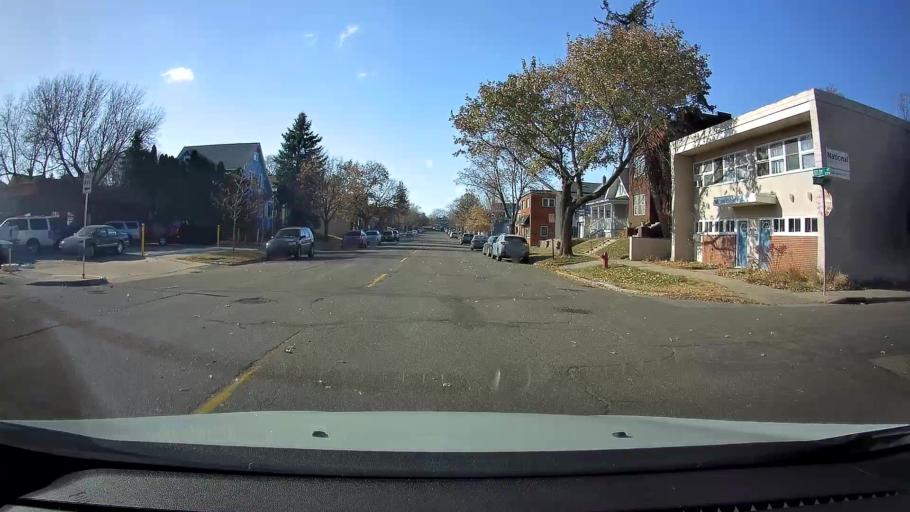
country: US
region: Minnesota
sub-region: Ramsey County
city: Falcon Heights
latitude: 44.9466
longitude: -93.1732
